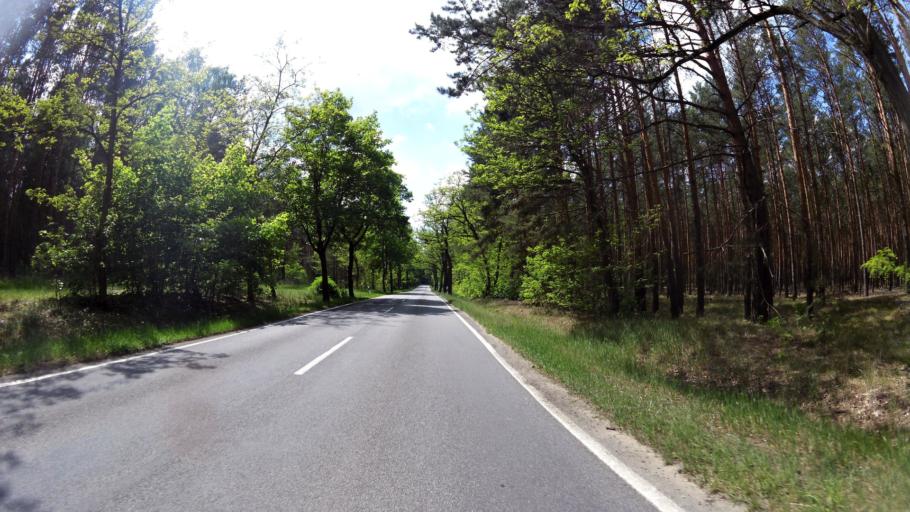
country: DE
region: Brandenburg
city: Gross Koris
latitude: 52.1649
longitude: 13.6782
